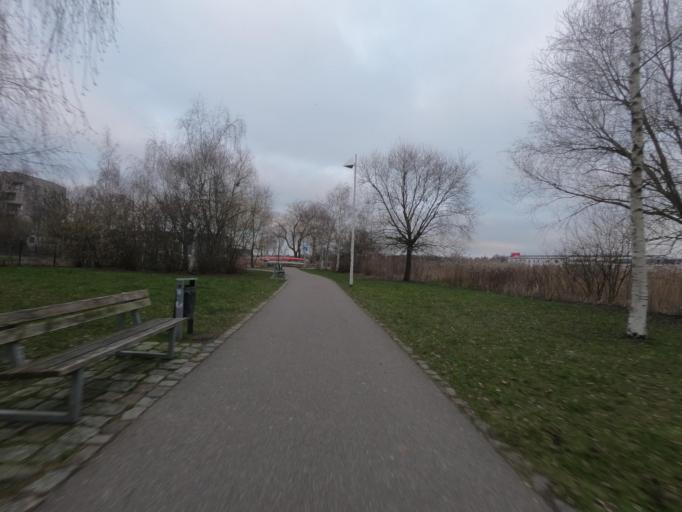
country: DE
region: Mecklenburg-Vorpommern
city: Rostock
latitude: 54.0933
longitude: 12.1520
